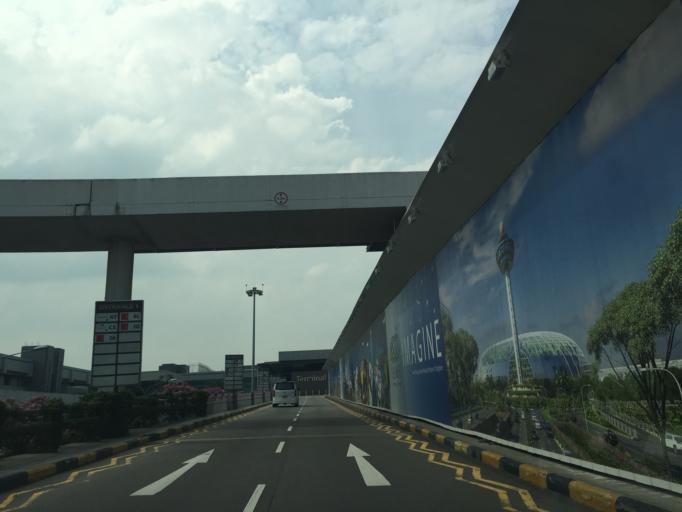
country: SG
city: Singapore
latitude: 1.3605
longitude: 103.9887
